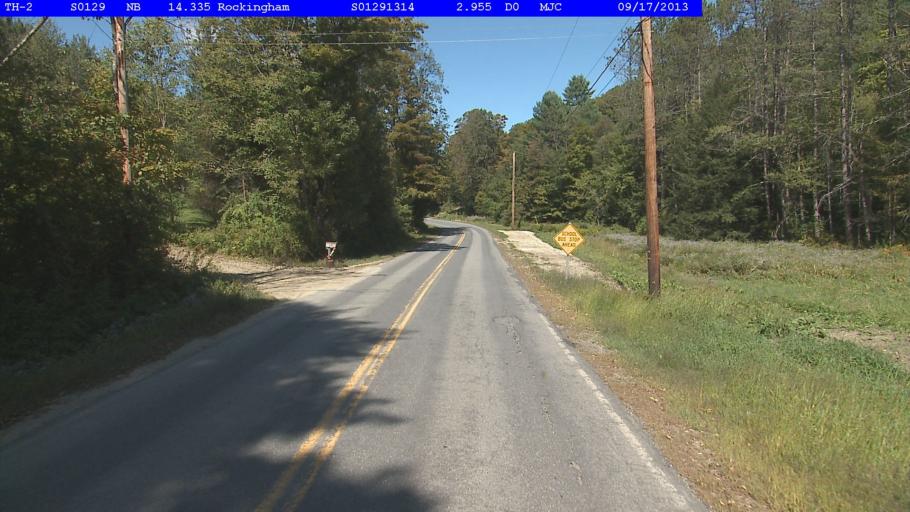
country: US
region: Vermont
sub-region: Windham County
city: Rockingham
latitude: 43.1599
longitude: -72.5176
